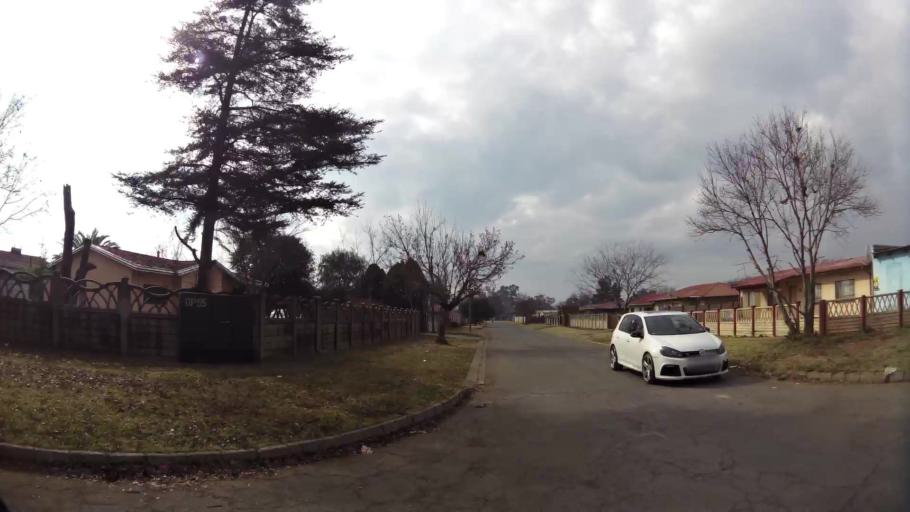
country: ZA
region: Gauteng
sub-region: Sedibeng District Municipality
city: Vanderbijlpark
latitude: -26.6771
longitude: 27.8342
